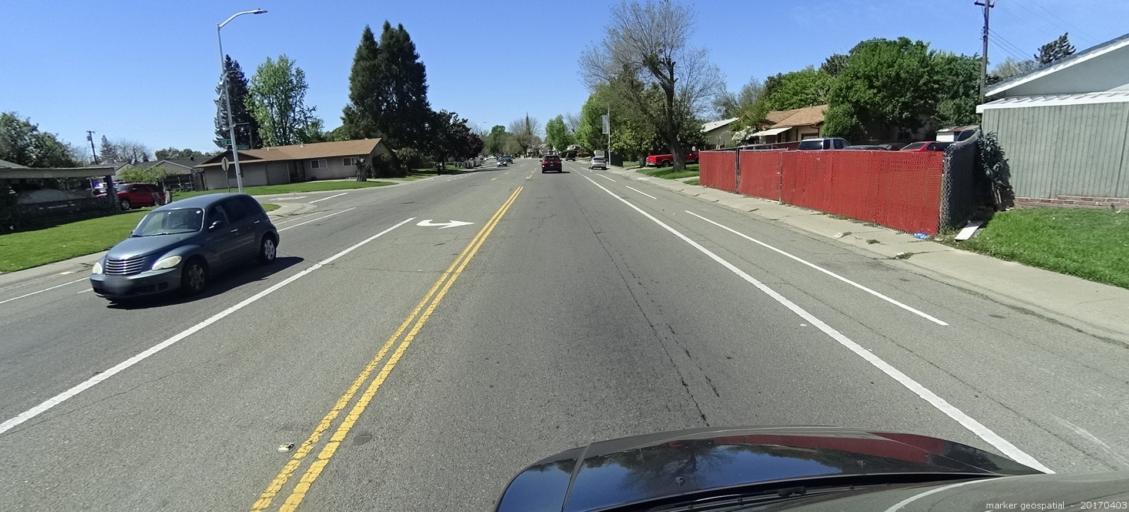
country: US
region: California
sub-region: Sacramento County
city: Sacramento
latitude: 38.6125
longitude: -121.4842
